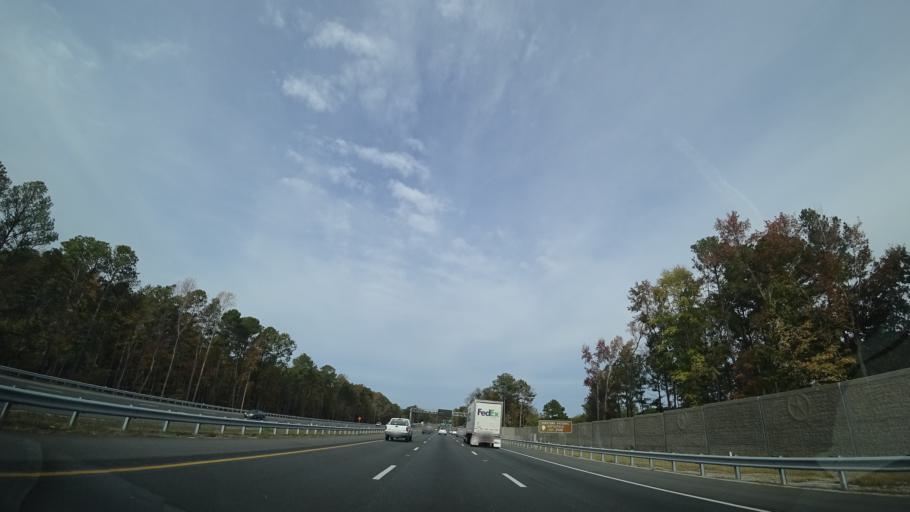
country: US
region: Virginia
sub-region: York County
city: Yorktown
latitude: 37.1663
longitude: -76.5462
